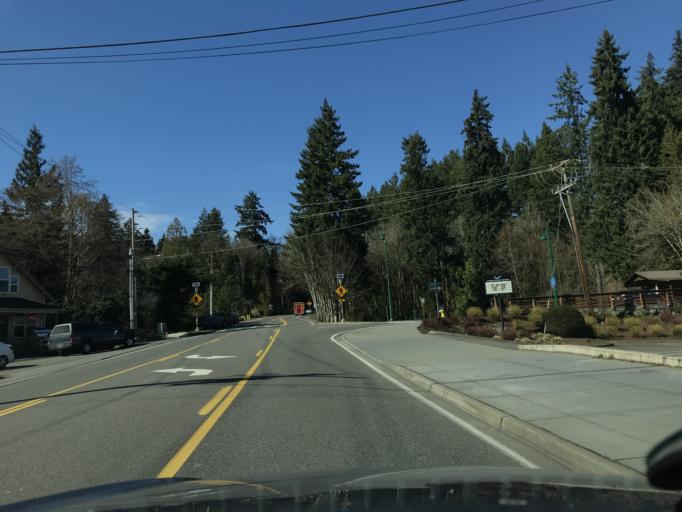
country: US
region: Washington
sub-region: Pierce County
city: Gig Harbor
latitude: 47.3369
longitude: -122.5937
